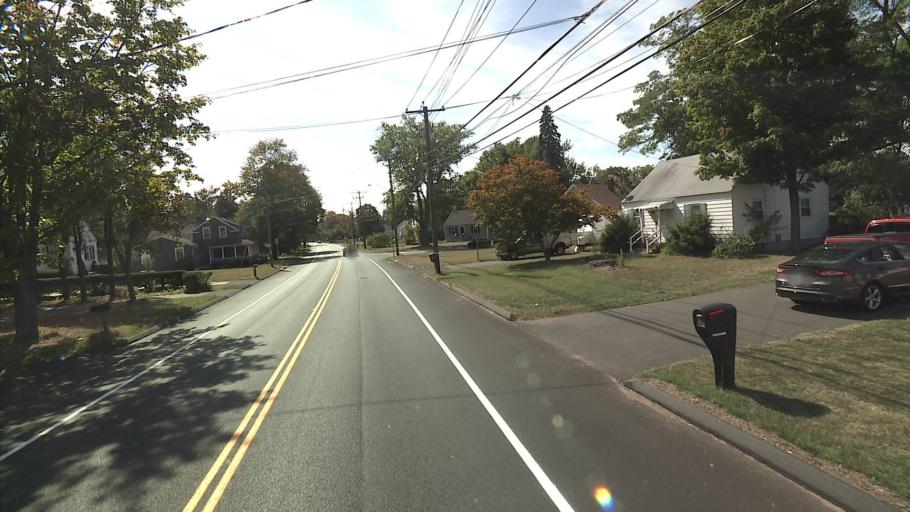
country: US
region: Connecticut
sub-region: New Haven County
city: North Haven
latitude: 41.3573
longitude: -72.8585
